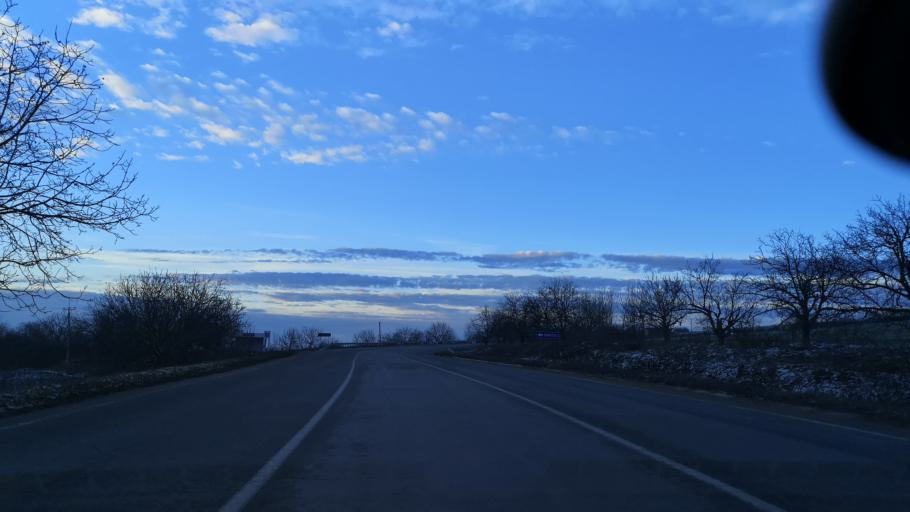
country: MD
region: Orhei
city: Orhei
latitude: 47.5239
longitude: 28.7978
